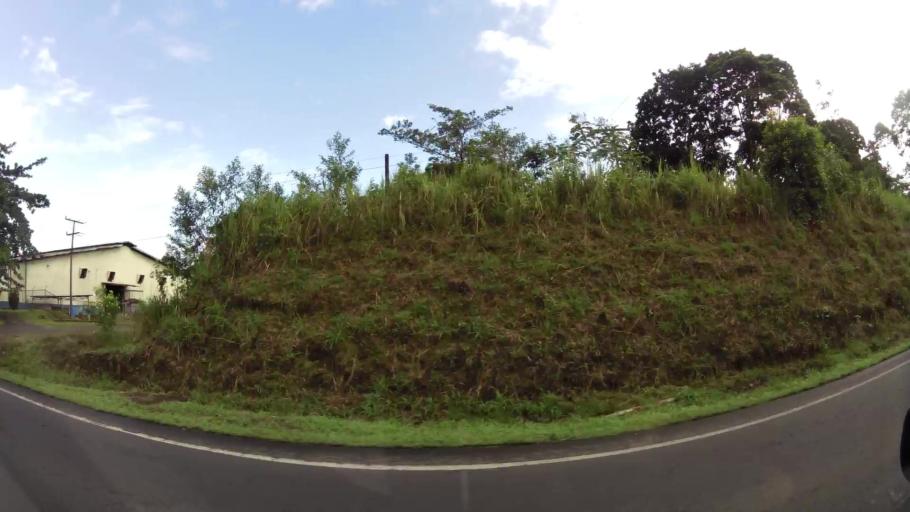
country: CR
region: Limon
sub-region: Canton de Guacimo
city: Guacimo
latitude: 10.2016
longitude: -83.6763
